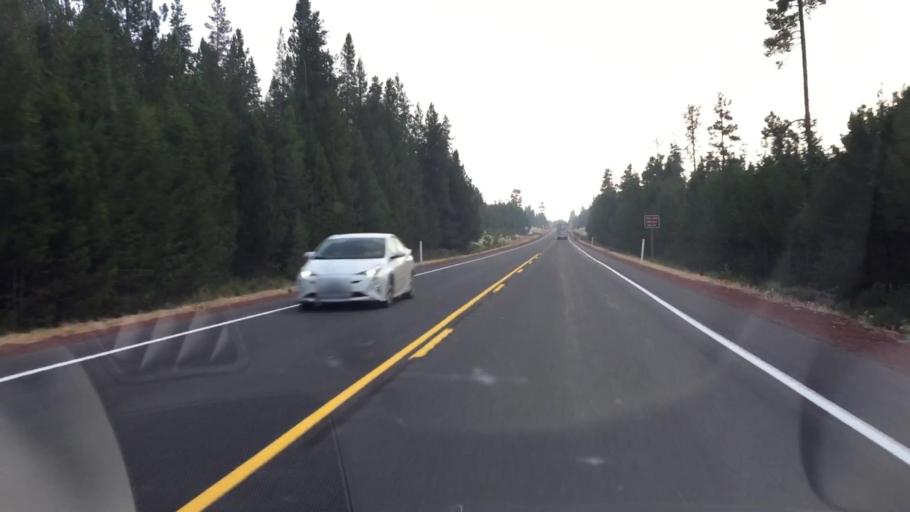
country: US
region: Oregon
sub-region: Deschutes County
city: La Pine
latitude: 43.3152
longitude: -121.7663
